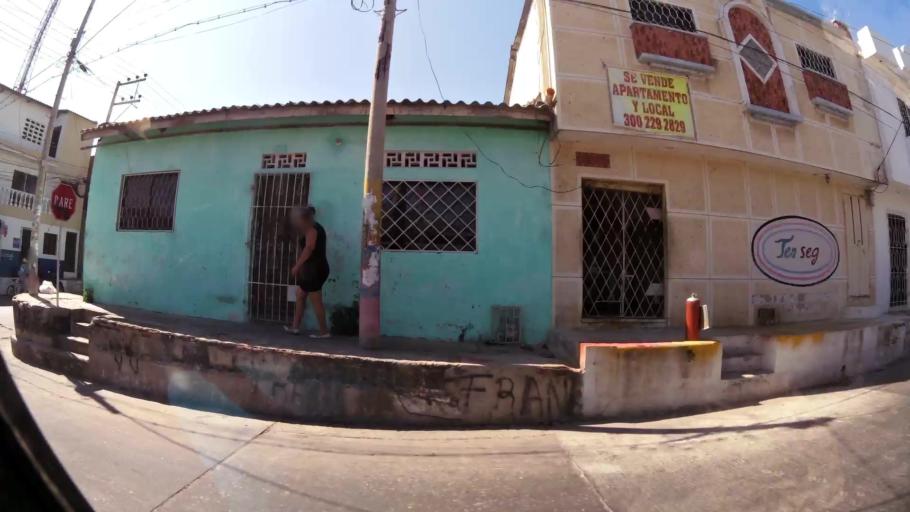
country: CO
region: Atlantico
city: Barranquilla
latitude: 10.9705
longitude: -74.7888
